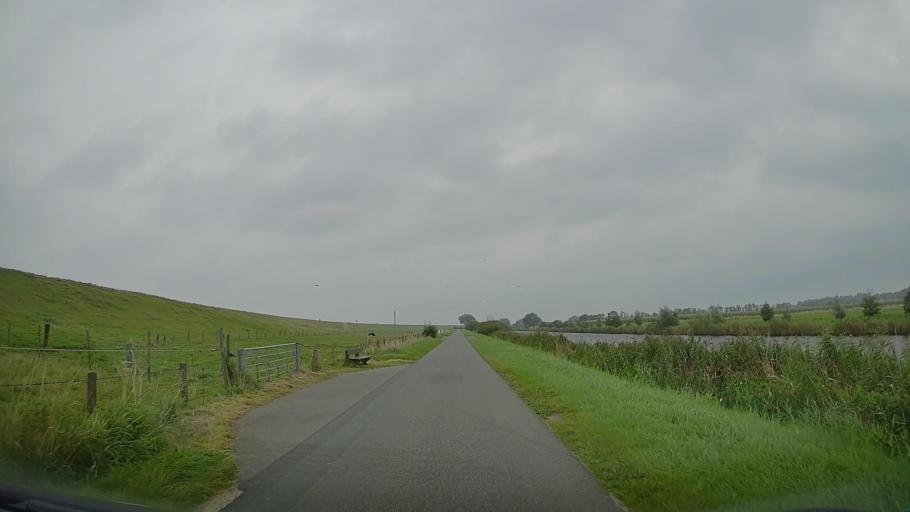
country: DE
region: Lower Saxony
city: Otterndorf
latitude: 53.8252
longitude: 8.9240
